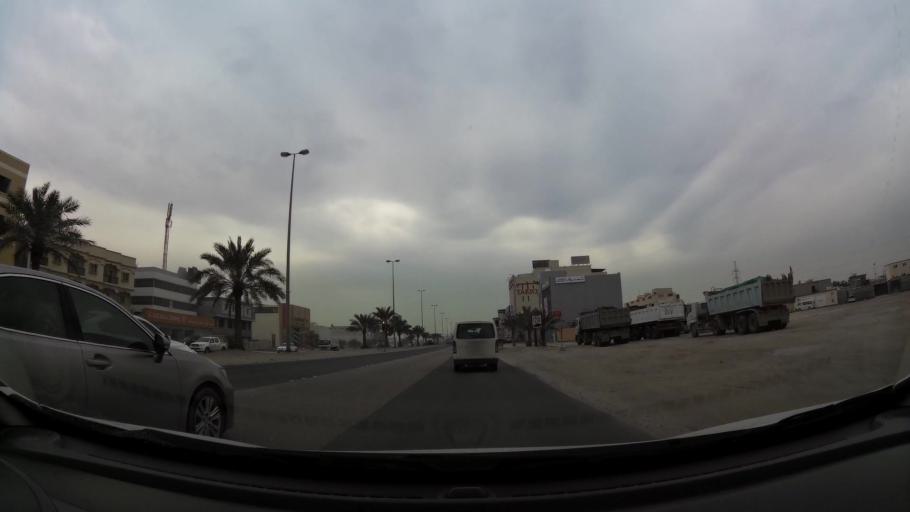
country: BH
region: Northern
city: Sitrah
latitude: 26.1401
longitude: 50.6129
